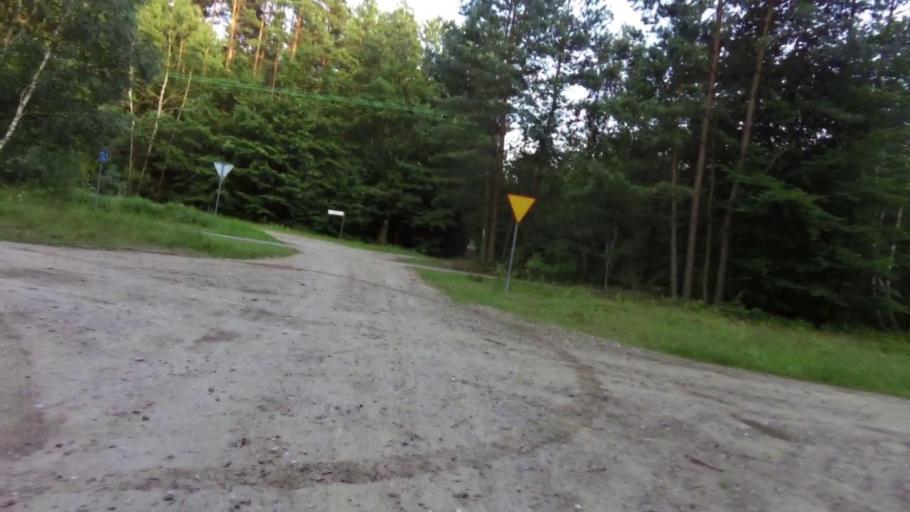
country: PL
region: West Pomeranian Voivodeship
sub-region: Powiat drawski
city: Zlocieniec
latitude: 53.5594
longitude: 16.0302
